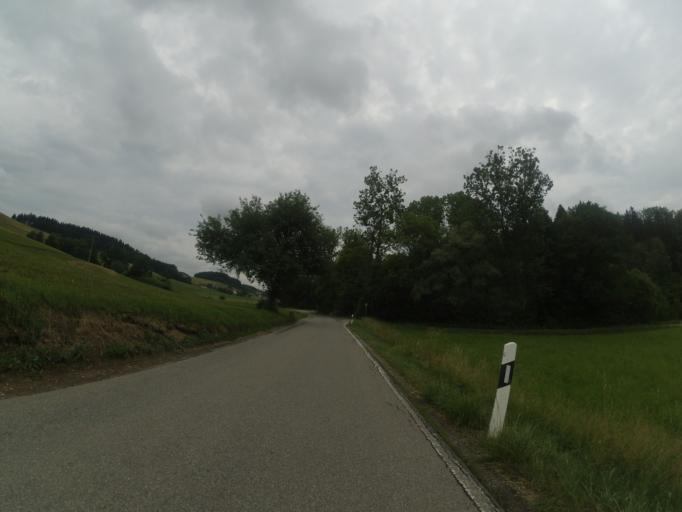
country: DE
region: Baden-Wuerttemberg
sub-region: Tuebingen Region
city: Wangen im Allgau
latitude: 47.6759
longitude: 9.8799
